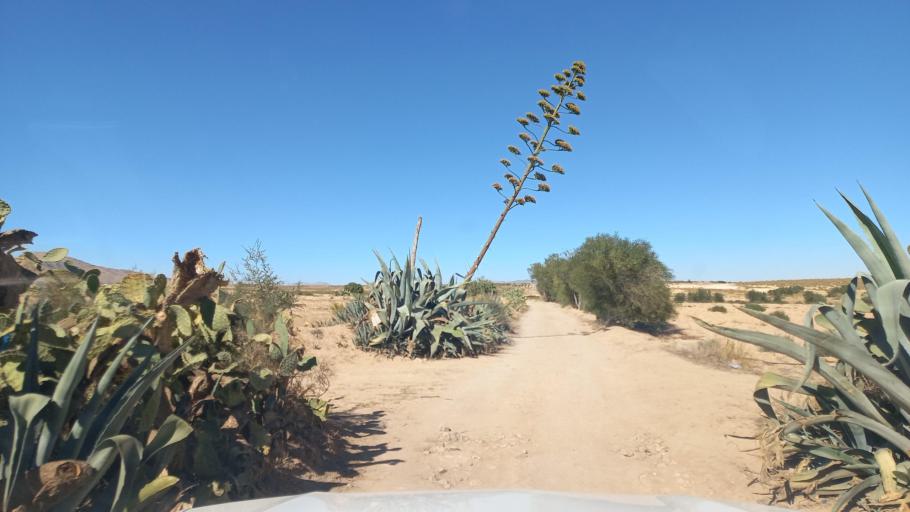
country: TN
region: Al Qasrayn
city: Sbiba
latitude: 35.4048
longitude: 9.0883
